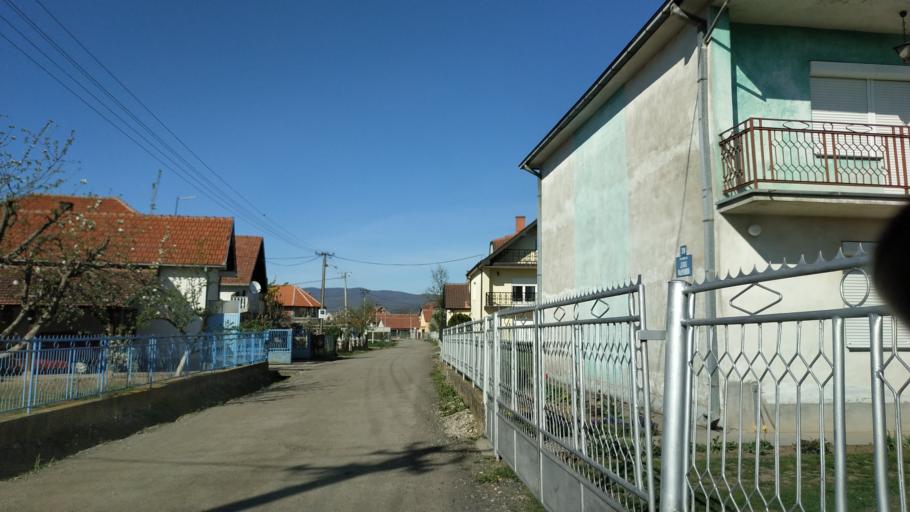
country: RS
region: Central Serbia
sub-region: Nisavski Okrug
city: Aleksinac
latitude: 43.5095
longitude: 21.6861
